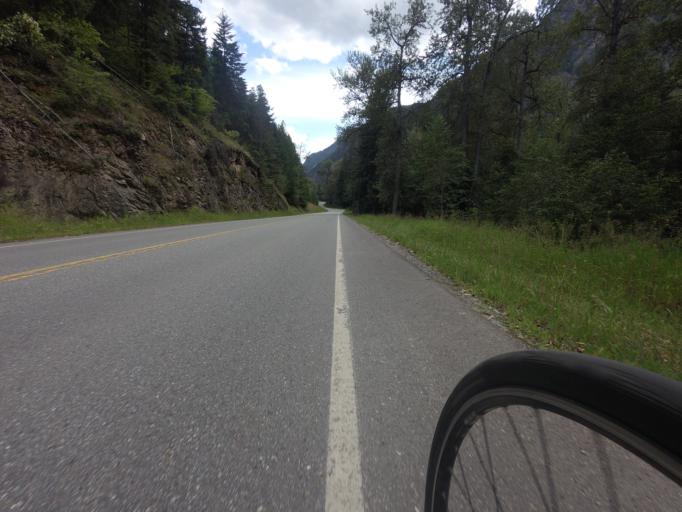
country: CA
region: British Columbia
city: Lillooet
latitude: 50.6210
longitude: -122.1034
